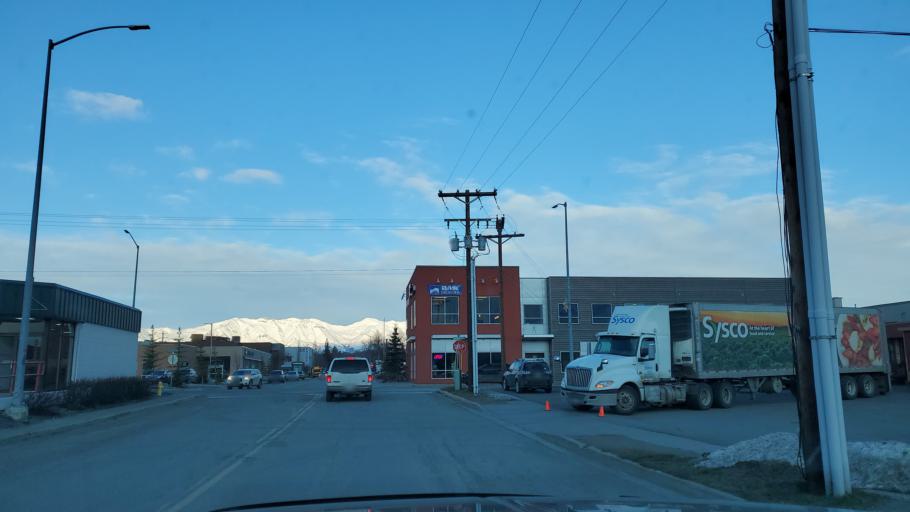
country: US
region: Alaska
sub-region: Matanuska-Susitna Borough
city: Palmer
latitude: 61.5990
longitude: -149.1164
